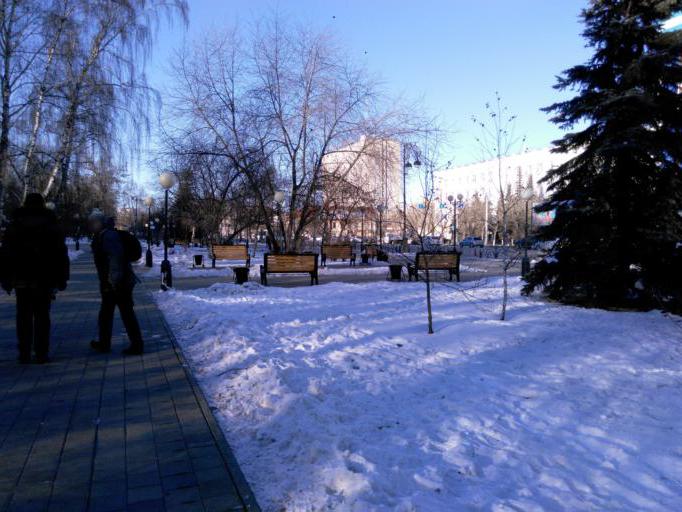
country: RU
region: Tjumen
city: Tyumen
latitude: 57.1394
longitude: 65.5660
